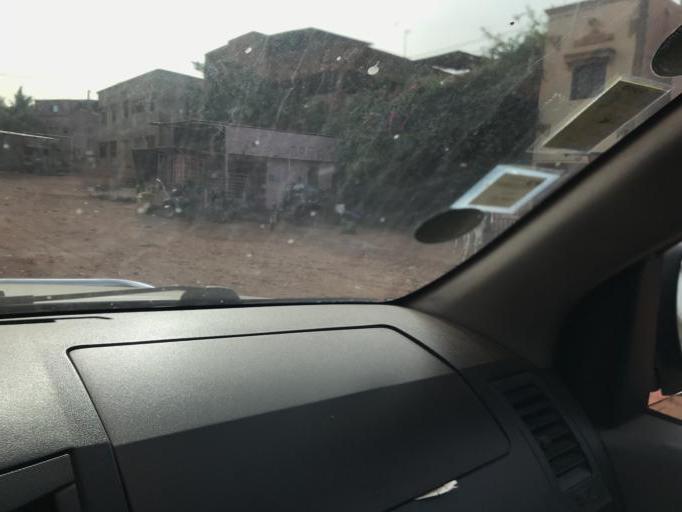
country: ML
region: Bamako
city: Bamako
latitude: 12.5816
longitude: -8.0015
